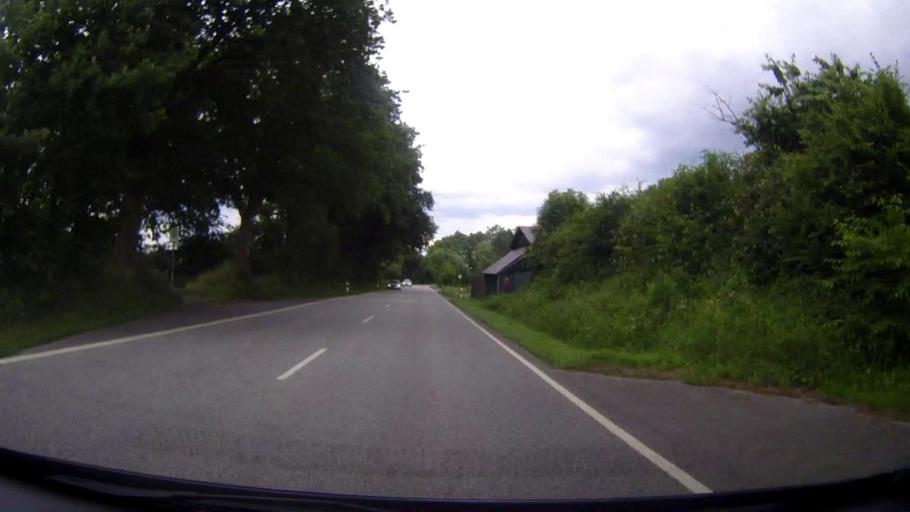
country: DE
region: Schleswig-Holstein
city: Oldenborstel
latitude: 54.0510
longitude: 9.5140
